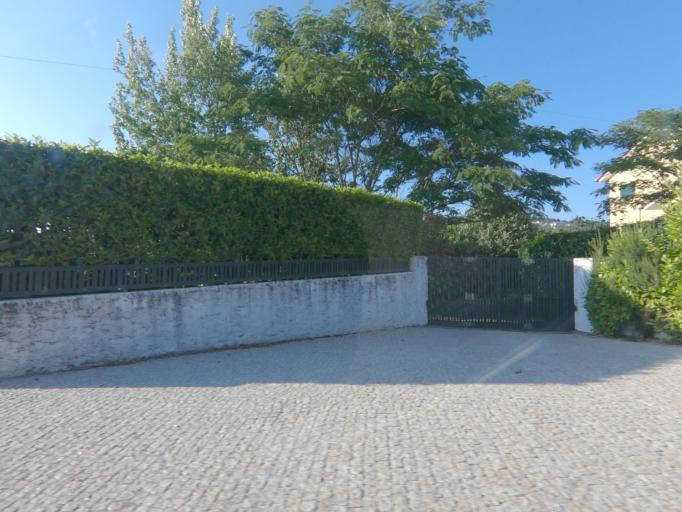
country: PT
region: Vila Real
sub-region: Sabrosa
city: Vilela
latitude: 41.2666
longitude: -7.6264
